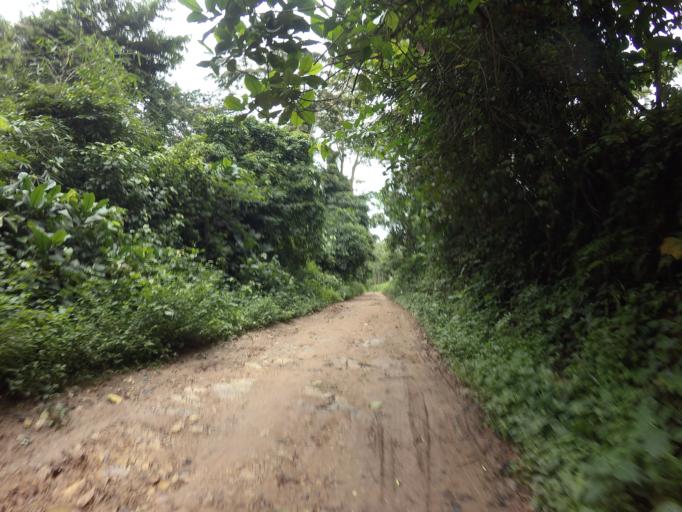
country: TG
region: Plateaux
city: Kpalime
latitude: 6.8449
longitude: 0.4391
